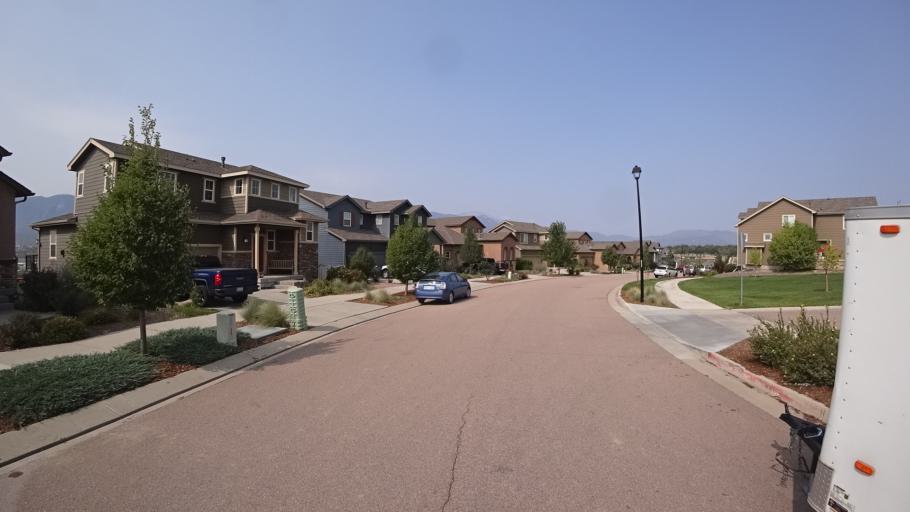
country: US
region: Colorado
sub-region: El Paso County
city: Stratmoor
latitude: 38.8069
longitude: -104.7893
